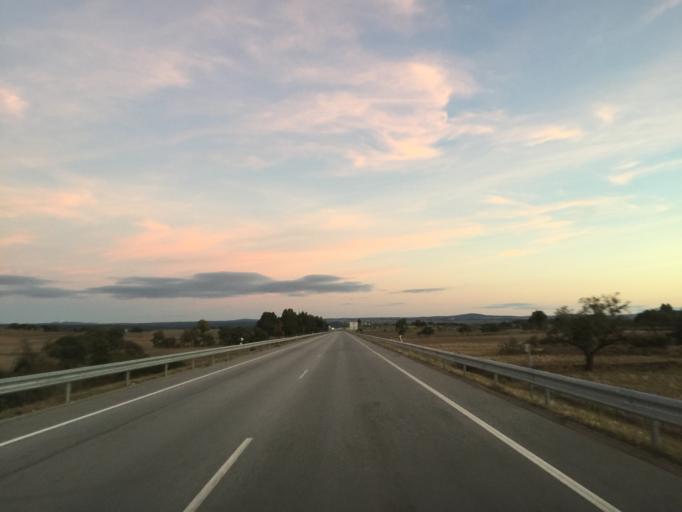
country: PT
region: Portalegre
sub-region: Alter do Chao
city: Alter do Chao
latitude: 39.3012
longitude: -7.6351
